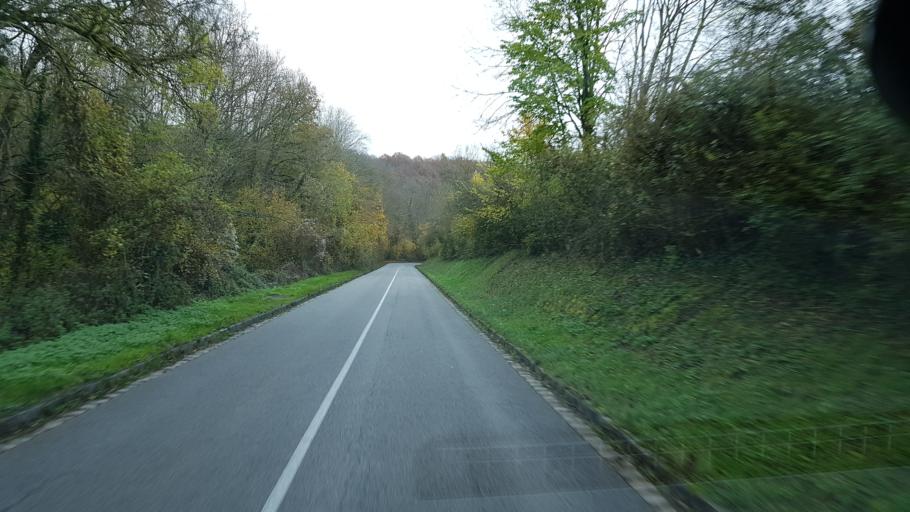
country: FR
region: Ile-de-France
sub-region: Departement des Yvelines
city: Chevreuse
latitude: 48.7170
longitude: 2.0172
